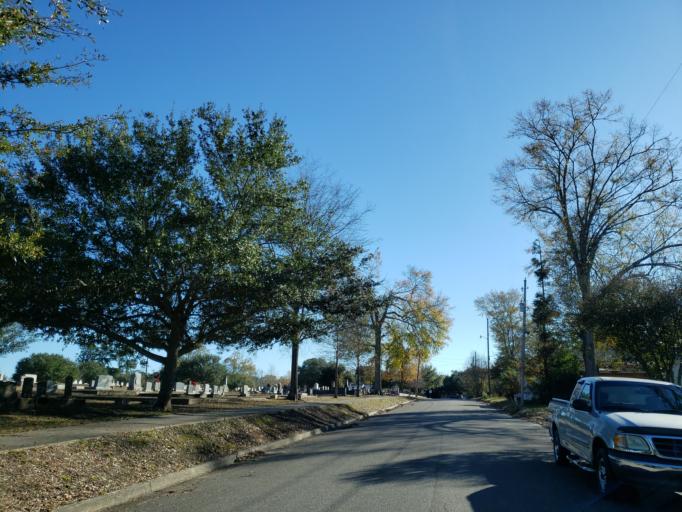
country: US
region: Mississippi
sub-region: Forrest County
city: Hattiesburg
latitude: 31.3266
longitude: -89.2993
